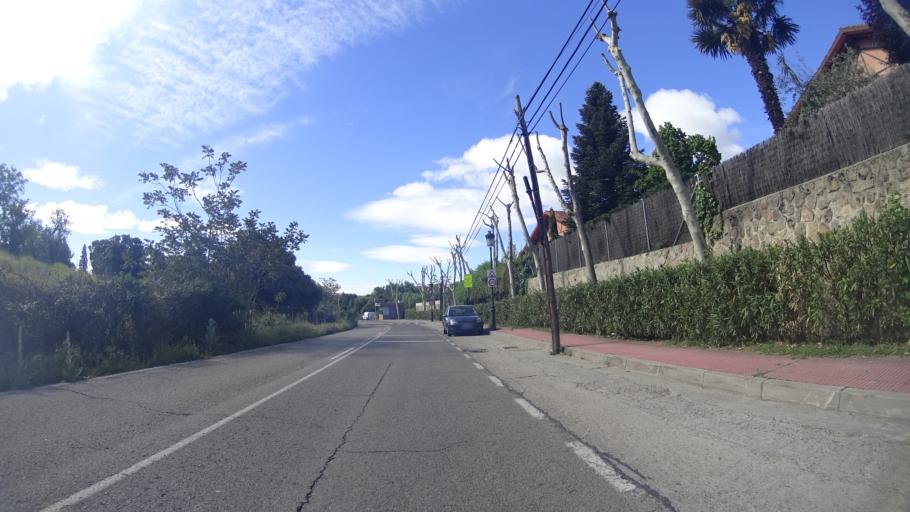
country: ES
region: Madrid
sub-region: Provincia de Madrid
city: Villanueva del Pardillo
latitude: 40.4633
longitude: -3.9461
